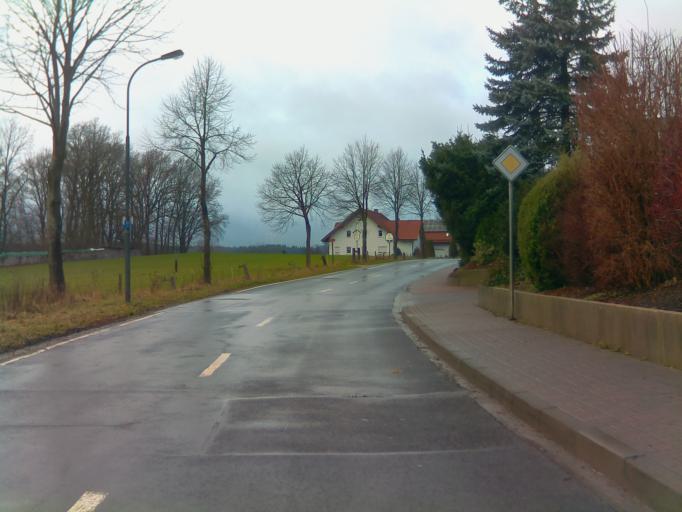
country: DE
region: Hesse
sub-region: Regierungsbezirk Kassel
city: Flieden
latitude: 50.4076
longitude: 9.5760
